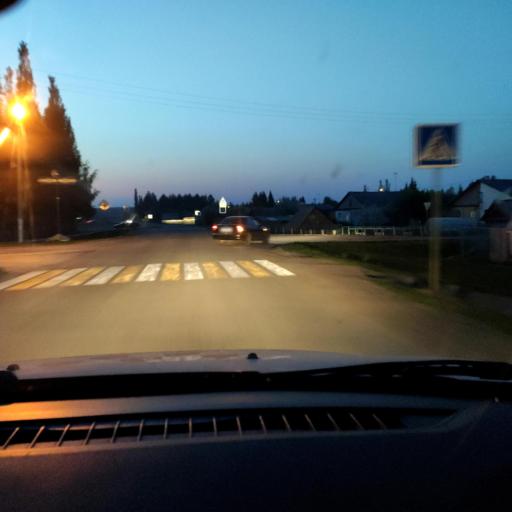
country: RU
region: Bashkortostan
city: Karmaskaly
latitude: 54.3653
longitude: 56.1580
